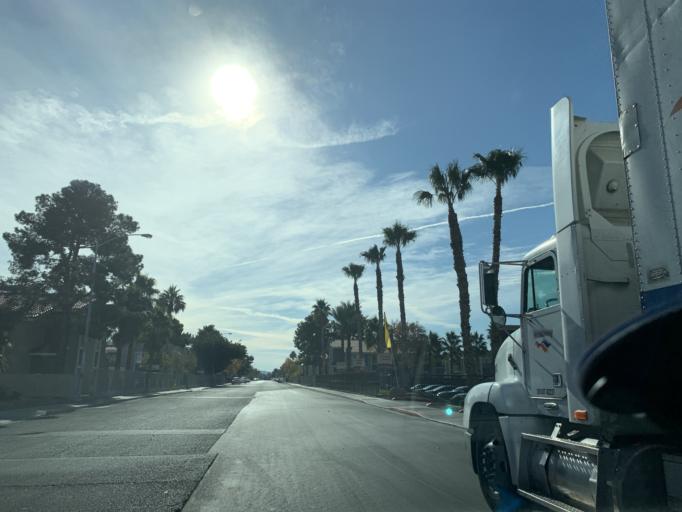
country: US
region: Nevada
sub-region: Clark County
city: Spring Valley
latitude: 36.0991
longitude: -115.2208
